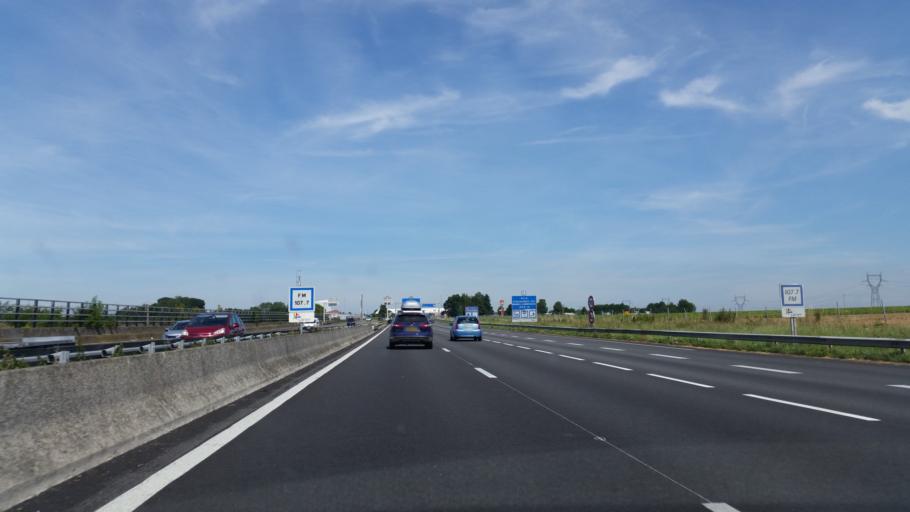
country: FR
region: Picardie
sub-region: Departement de la Somme
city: Chaulnes
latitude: 49.8808
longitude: 2.8373
